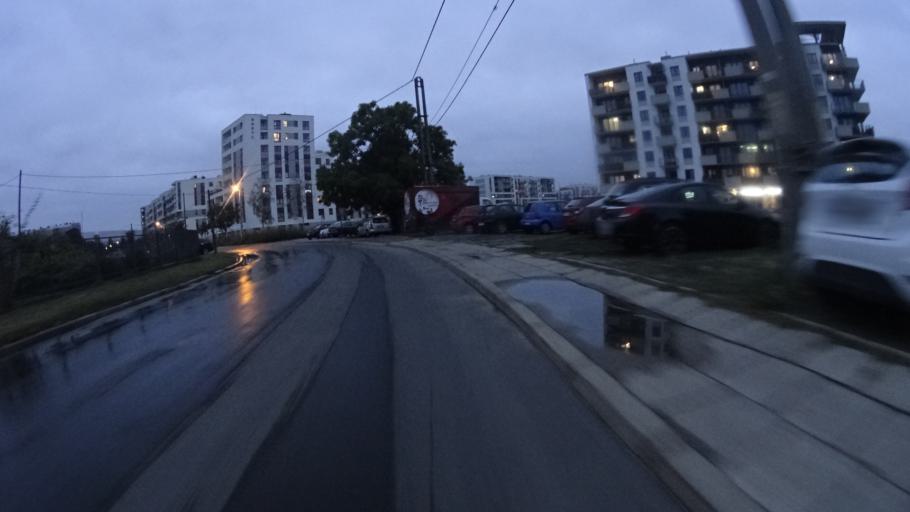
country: PL
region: Masovian Voivodeship
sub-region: Warszawa
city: Ursus
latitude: 52.2269
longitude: 20.8902
